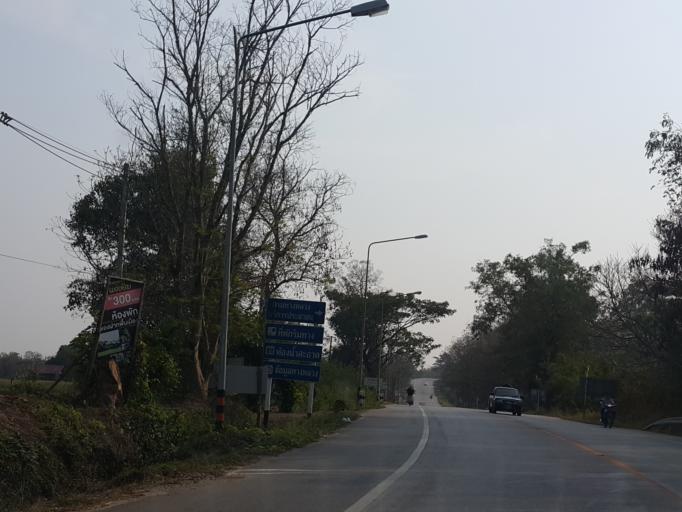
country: TH
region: Lampang
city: Chae Hom
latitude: 18.7200
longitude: 99.5619
